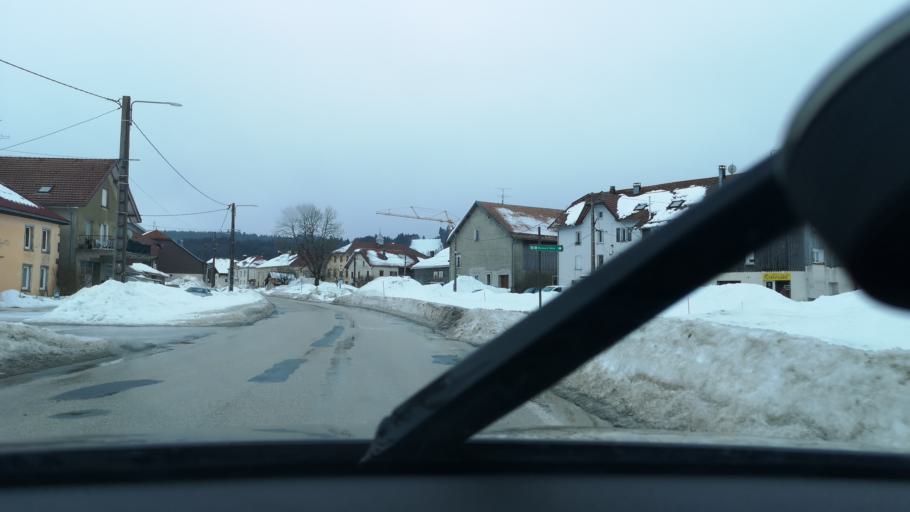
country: FR
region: Franche-Comte
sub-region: Departement du Doubs
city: Les Fourgs
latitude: 46.8366
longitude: 6.3980
